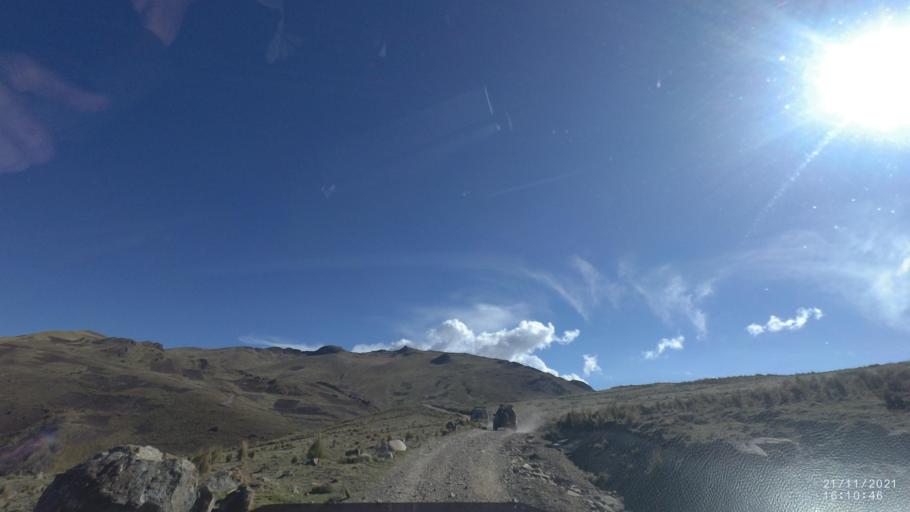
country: BO
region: Cochabamba
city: Cochabamba
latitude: -16.9937
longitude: -66.2705
